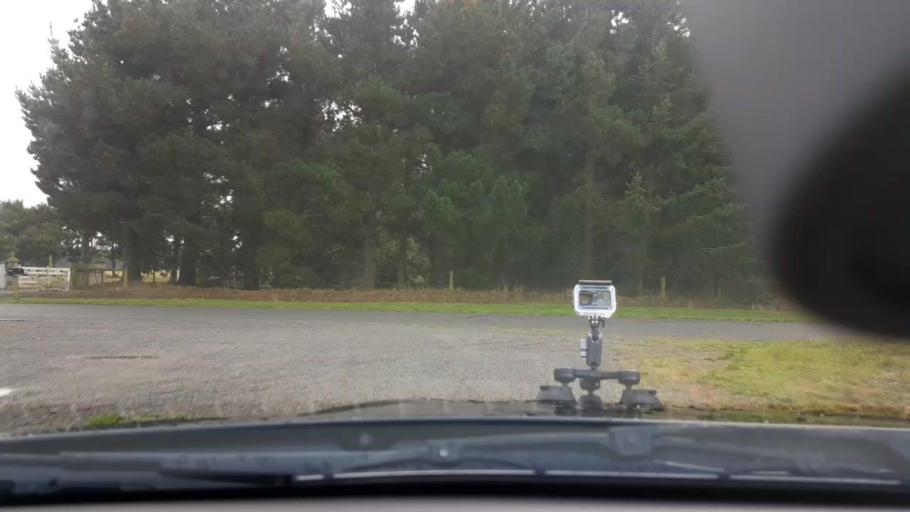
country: NZ
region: Canterbury
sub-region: Waimakariri District
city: Oxford
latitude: -43.3988
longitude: 172.3132
